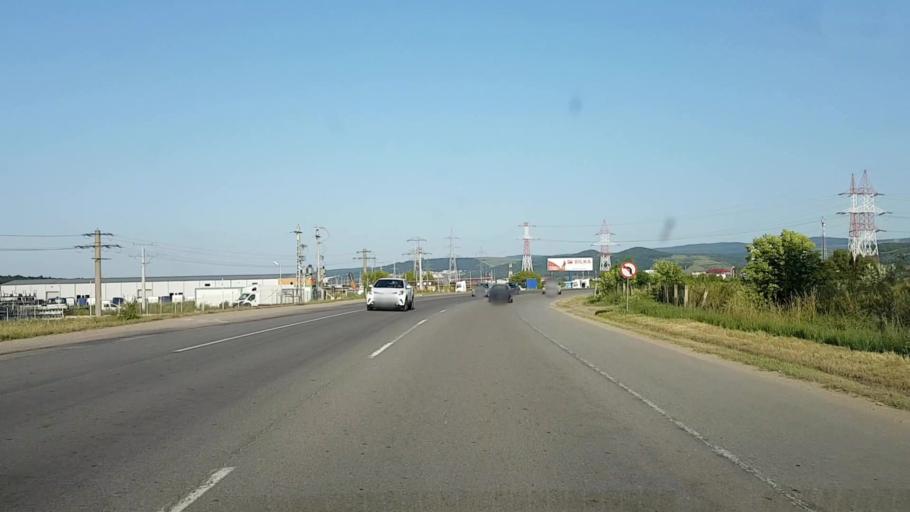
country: RO
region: Cluj
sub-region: Comuna Floresti
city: Luna de Sus
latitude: 46.7501
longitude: 23.4416
